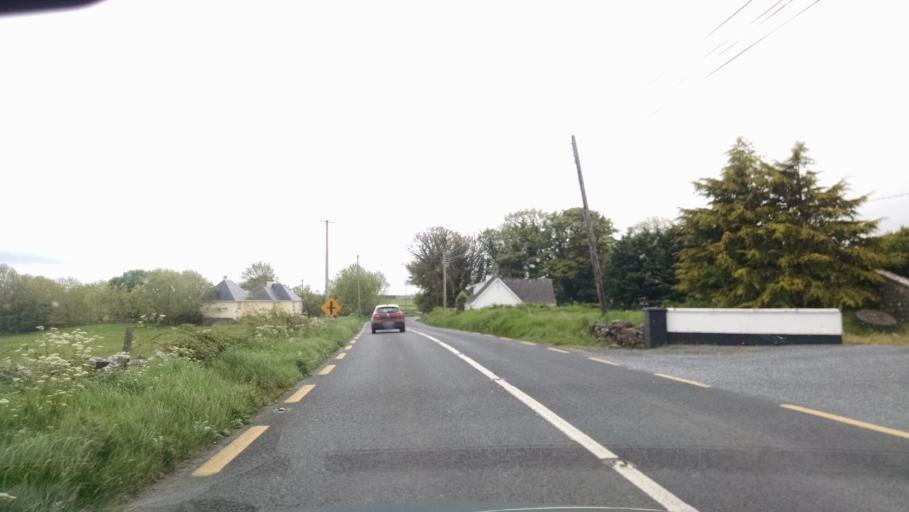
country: IE
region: Connaught
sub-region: County Galway
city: Moycullen
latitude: 53.5004
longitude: -9.0798
